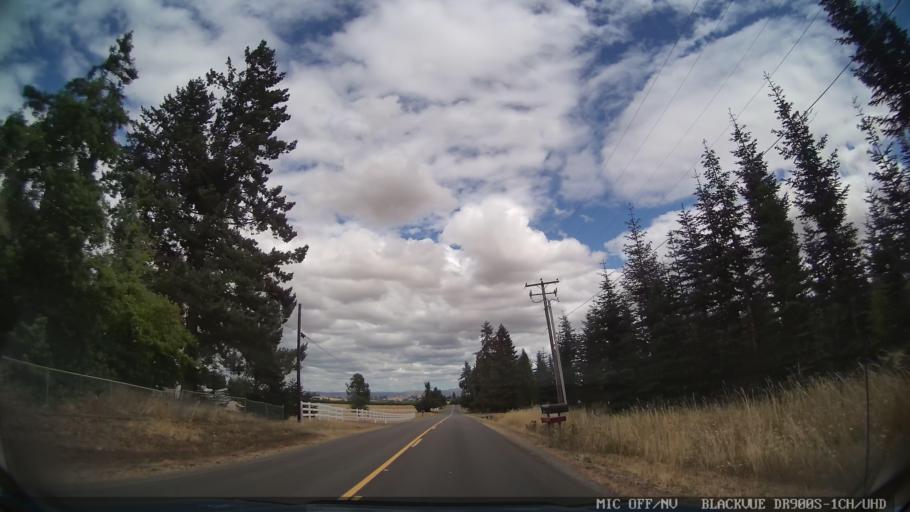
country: US
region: Oregon
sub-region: Marion County
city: Aumsville
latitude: 44.8604
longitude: -122.8590
